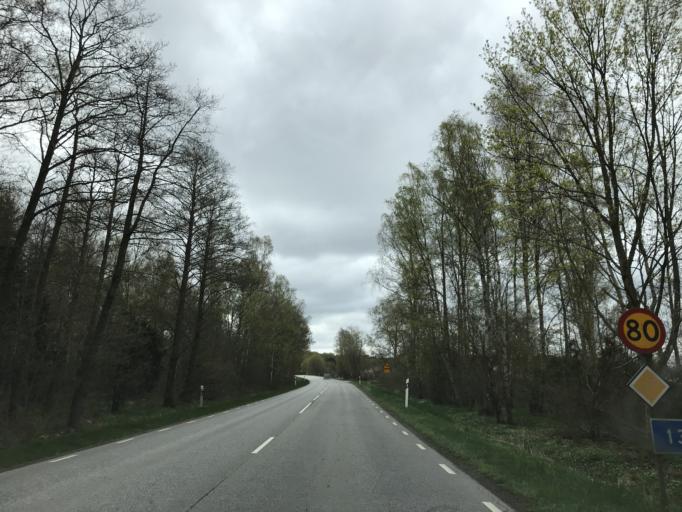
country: SE
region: Skane
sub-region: Hoors Kommun
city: Hoeoer
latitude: 55.9458
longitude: 13.4612
